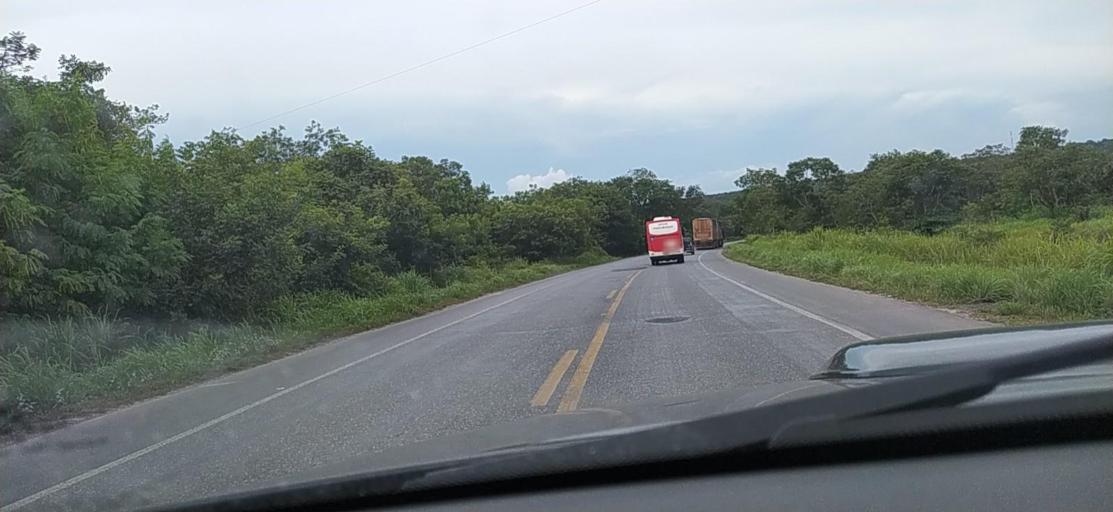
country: BR
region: Minas Gerais
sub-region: Montes Claros
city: Montes Claros
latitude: -16.6653
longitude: -43.7849
